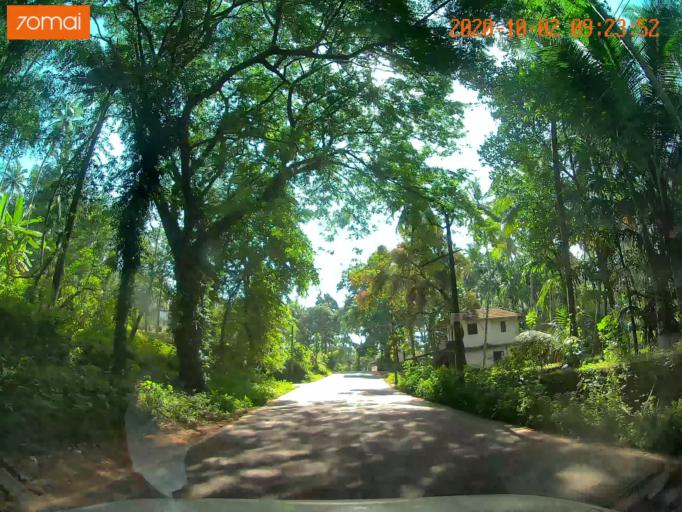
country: IN
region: Kerala
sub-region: Kozhikode
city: Naduvannur
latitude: 11.5834
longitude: 75.7610
